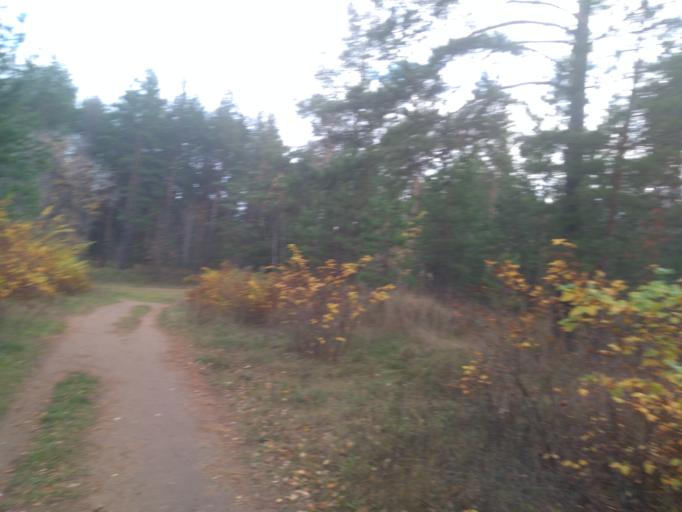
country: RU
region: Tatarstan
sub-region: Tukayevskiy Rayon
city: Naberezhnyye Chelny
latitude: 55.7574
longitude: 52.3775
